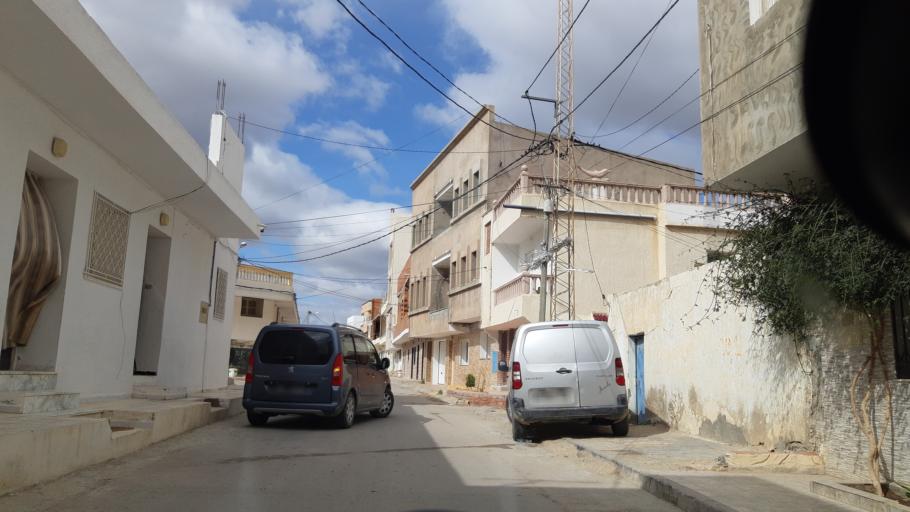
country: TN
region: Susah
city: Akouda
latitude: 35.8706
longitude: 10.5265
